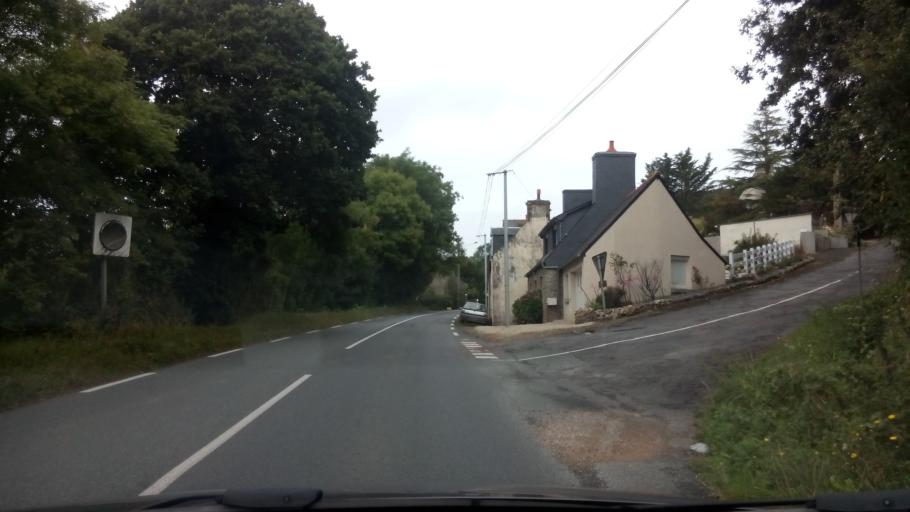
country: FR
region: Brittany
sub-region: Departement des Cotes-d'Armor
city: Locquemeau
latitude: 48.6891
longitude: -3.5603
